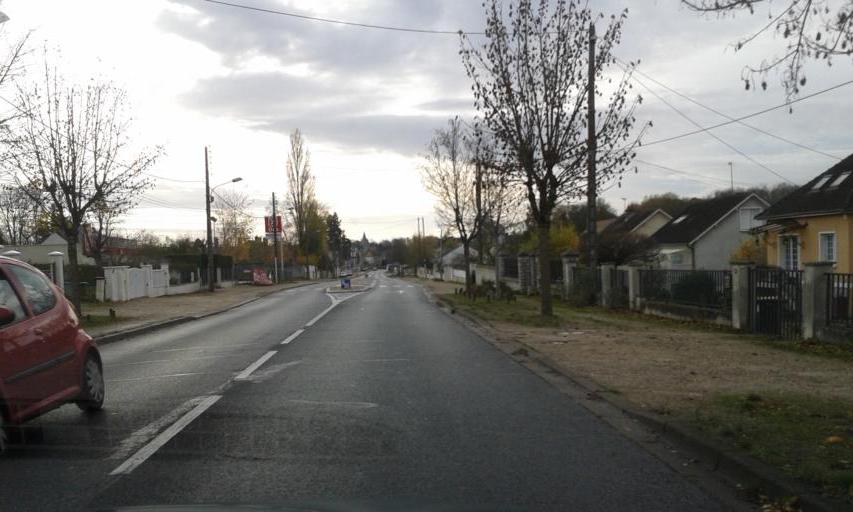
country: FR
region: Centre
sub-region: Departement du Loiret
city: Meung-sur-Loire
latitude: 47.8322
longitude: 1.7038
